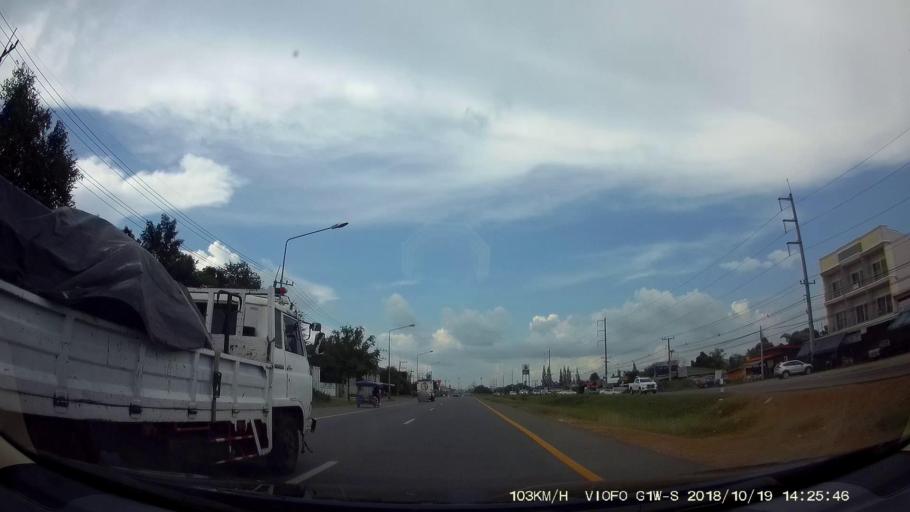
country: TH
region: Chaiyaphum
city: Kaeng Khro
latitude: 16.0983
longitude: 102.2628
